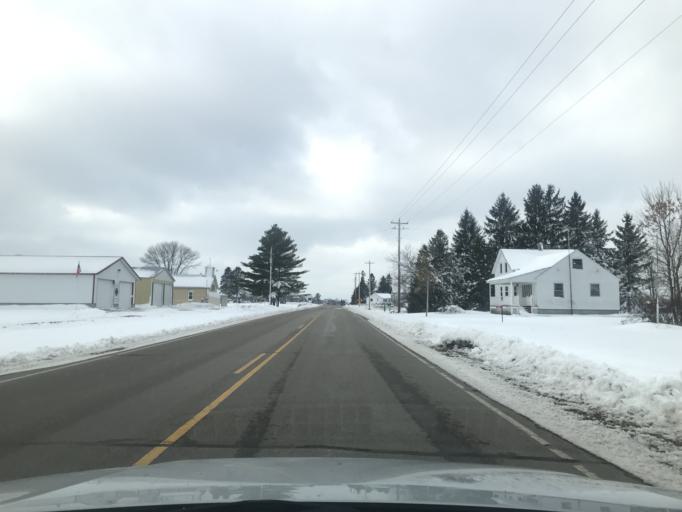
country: US
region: Wisconsin
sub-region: Oconto County
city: Oconto
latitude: 44.9497
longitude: -87.9418
